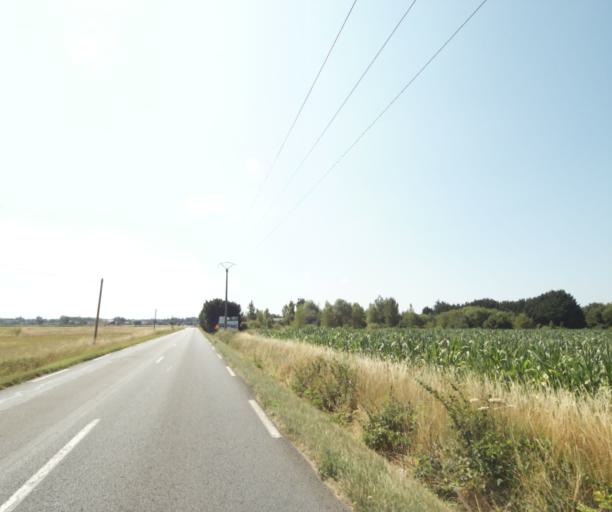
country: FR
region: Centre
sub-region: Departement du Loiret
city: Saint-Cyr-en-Val
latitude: 47.8409
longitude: 1.9619
